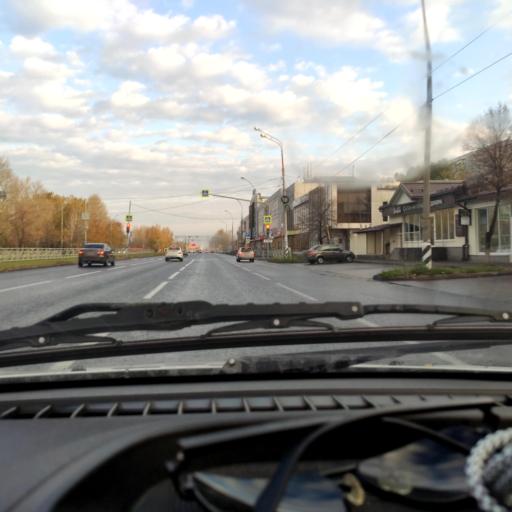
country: RU
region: Samara
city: Tol'yatti
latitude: 53.5345
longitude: 49.2832
